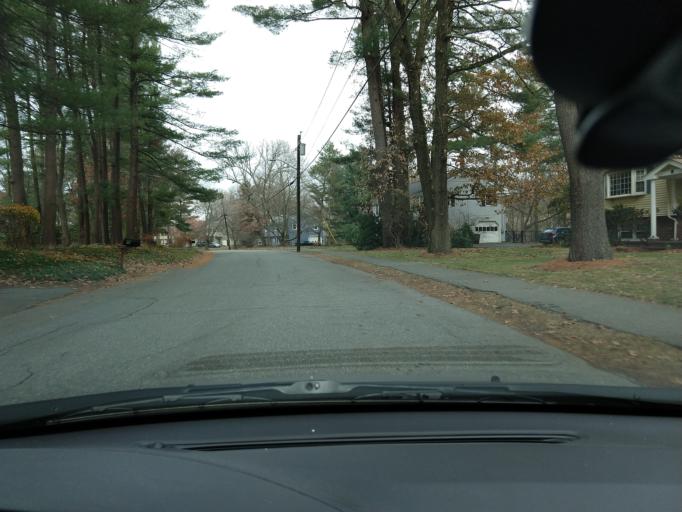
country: US
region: Massachusetts
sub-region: Middlesex County
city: Bedford
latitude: 42.5046
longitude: -71.2482
